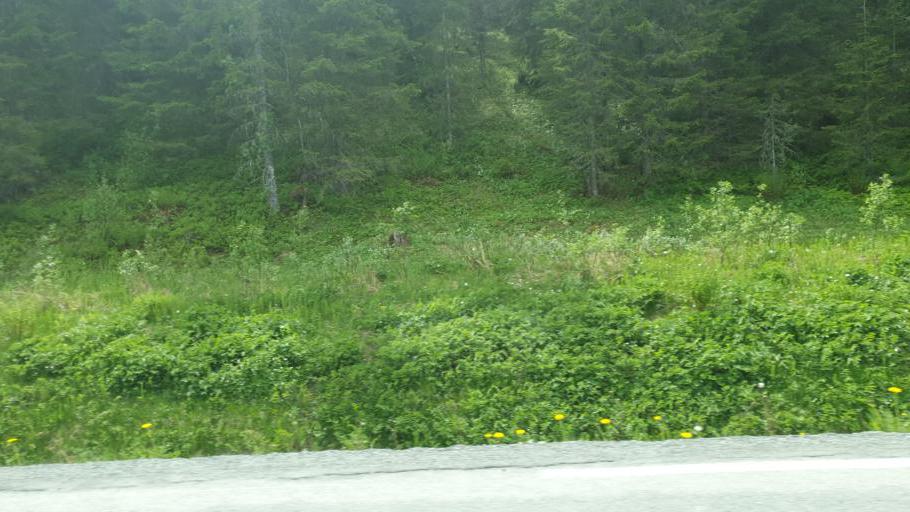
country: NO
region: Nord-Trondelag
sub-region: Leksvik
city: Leksvik
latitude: 63.6904
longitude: 10.5206
